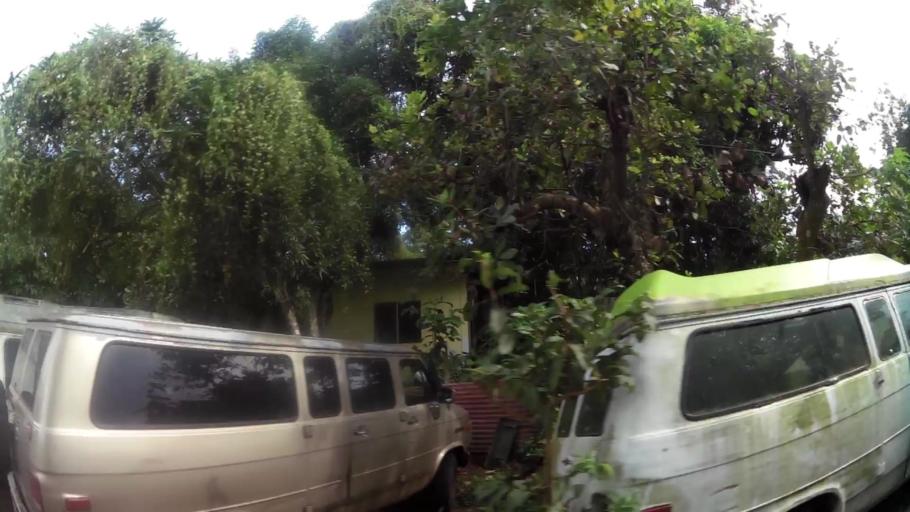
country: PA
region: Panama
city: El Coco
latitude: 8.8716
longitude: -79.8052
